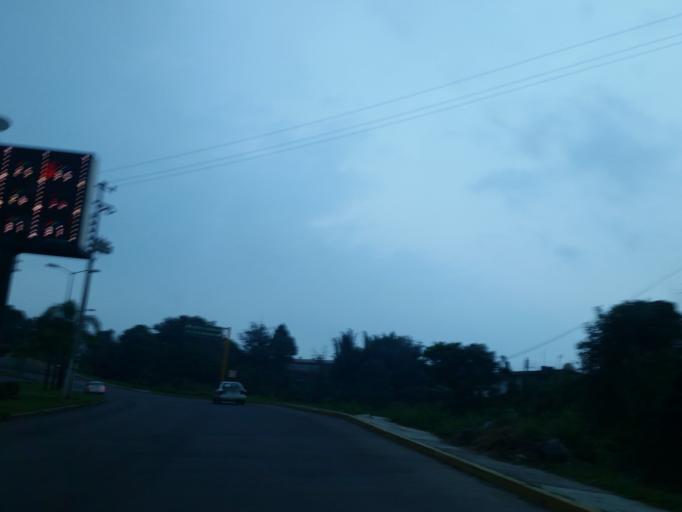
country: MX
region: Veracruz
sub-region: Xalapa
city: Xalapa de Enriquez
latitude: 19.5236
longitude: -96.9076
